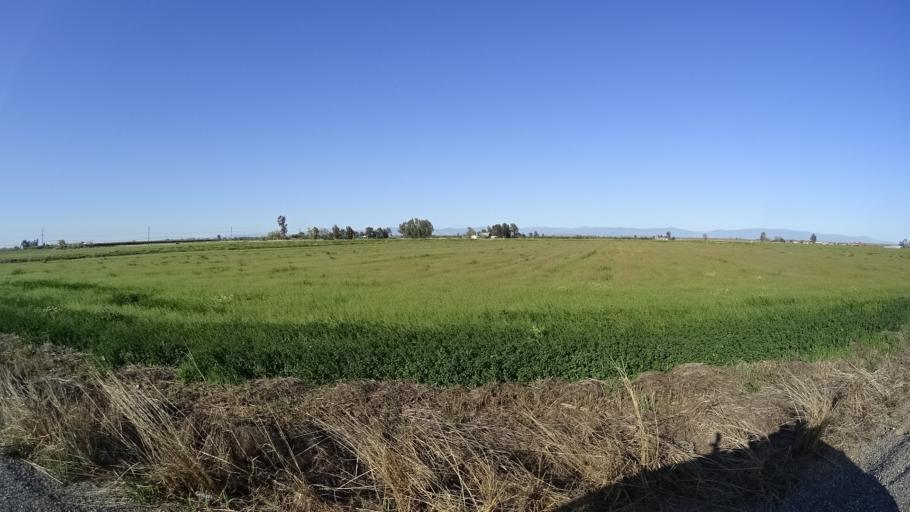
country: US
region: California
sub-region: Glenn County
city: Orland
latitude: 39.7711
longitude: -122.1114
